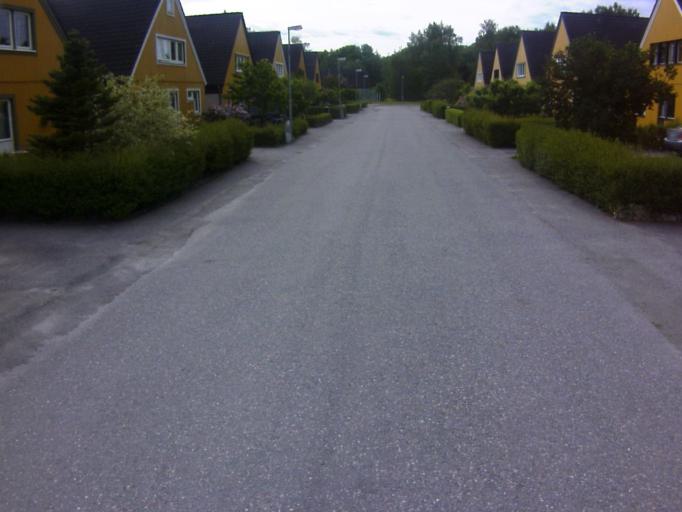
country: SE
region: Soedermanland
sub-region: Eskilstuna Kommun
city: Skogstorp
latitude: 59.3189
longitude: 16.4817
